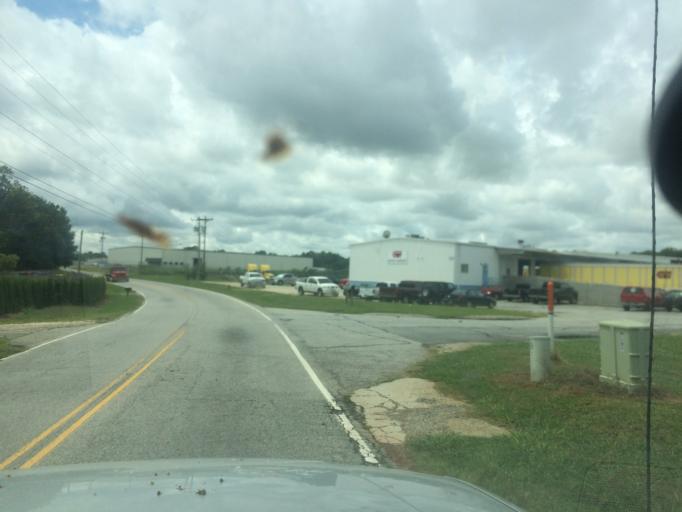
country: US
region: South Carolina
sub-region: Spartanburg County
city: Duncan
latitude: 34.8907
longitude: -82.1432
